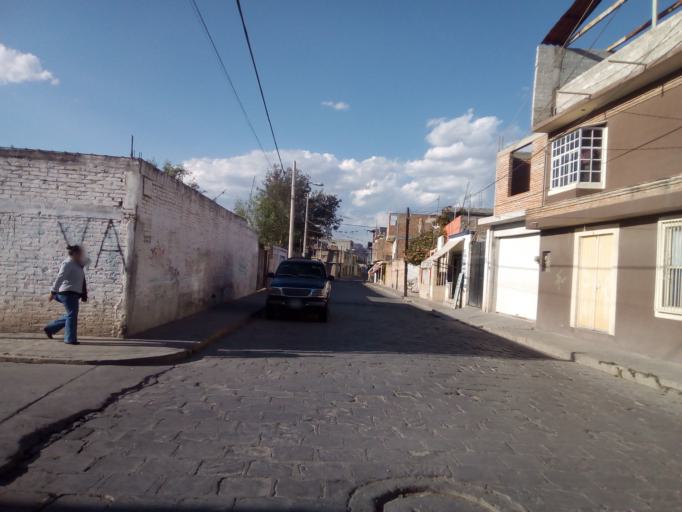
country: MX
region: Guerrero
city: San Luis de la Paz
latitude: 21.3008
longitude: -100.5220
